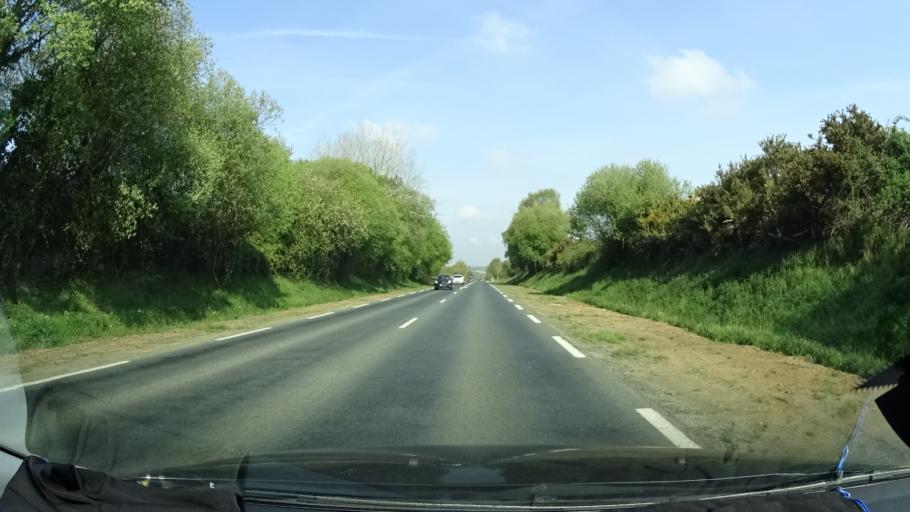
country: FR
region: Brittany
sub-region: Departement des Cotes-d'Armor
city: Lantic
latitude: 48.5621
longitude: -2.8922
